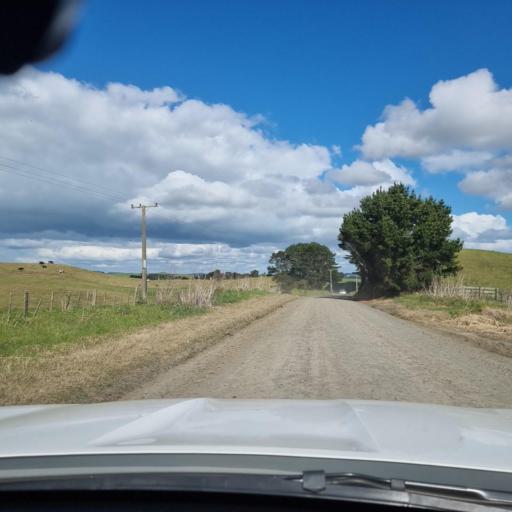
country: NZ
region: Auckland
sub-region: Auckland
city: Wellsford
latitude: -36.3202
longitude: 174.1347
